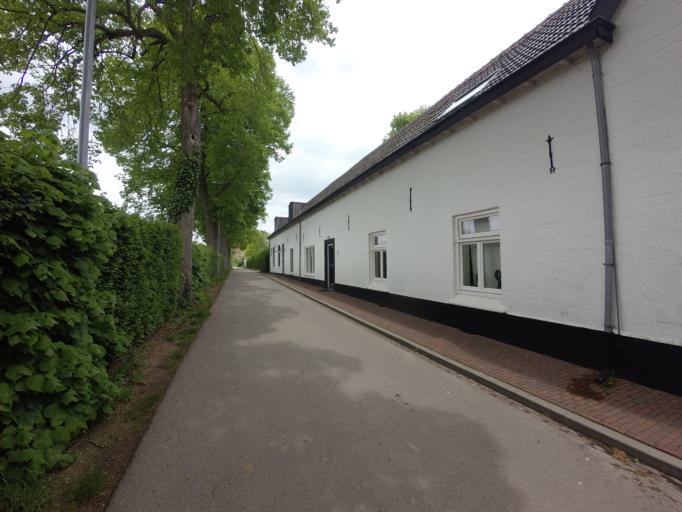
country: NL
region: Limburg
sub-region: Gemeente Maastricht
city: Heer
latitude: 50.8364
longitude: 5.7488
